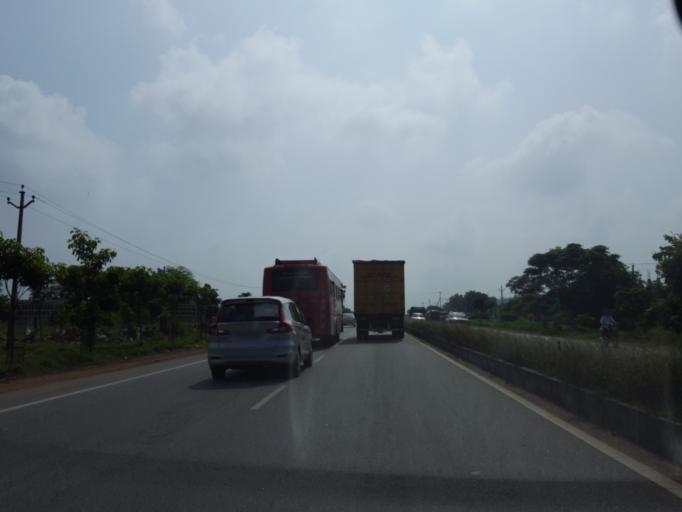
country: IN
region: Telangana
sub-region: Rangareddi
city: Ghatkesar
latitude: 17.2902
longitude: 78.7660
